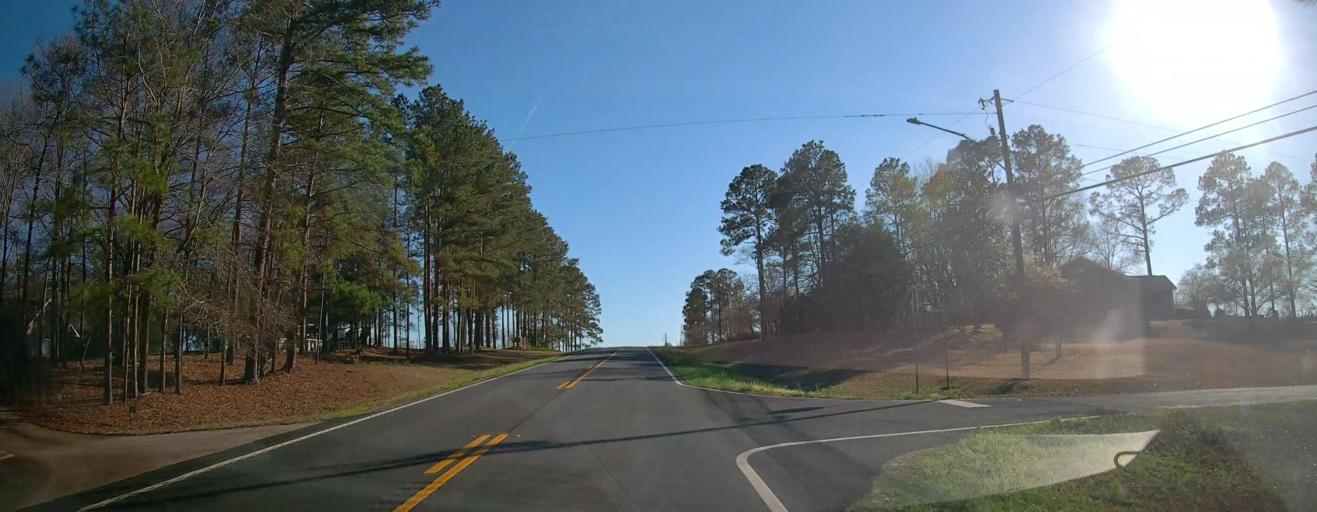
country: US
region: Georgia
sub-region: Taylor County
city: Reynolds
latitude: 32.5500
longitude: -84.0986
